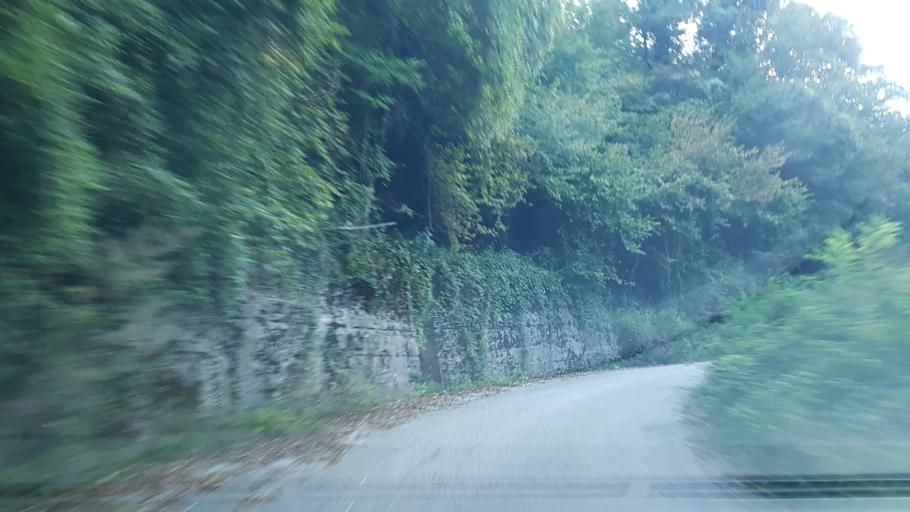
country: IT
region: Friuli Venezia Giulia
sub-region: Provincia di Udine
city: Venzone
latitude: 46.3356
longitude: 13.1662
